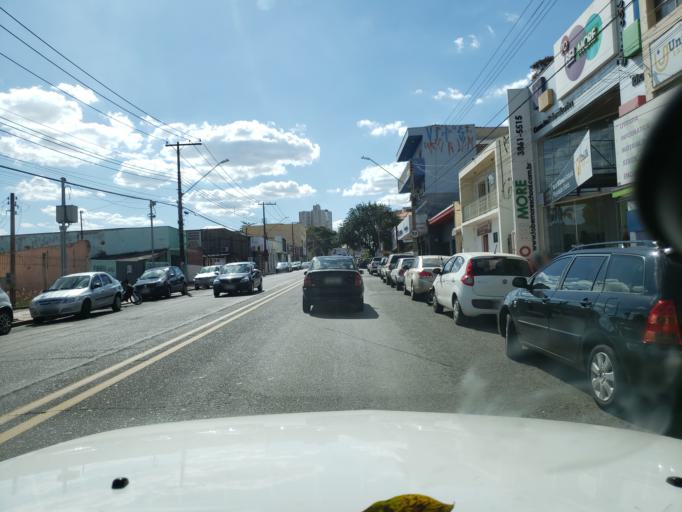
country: BR
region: Sao Paulo
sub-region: Moji-Guacu
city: Mogi-Gaucu
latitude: -22.3689
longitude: -46.9455
